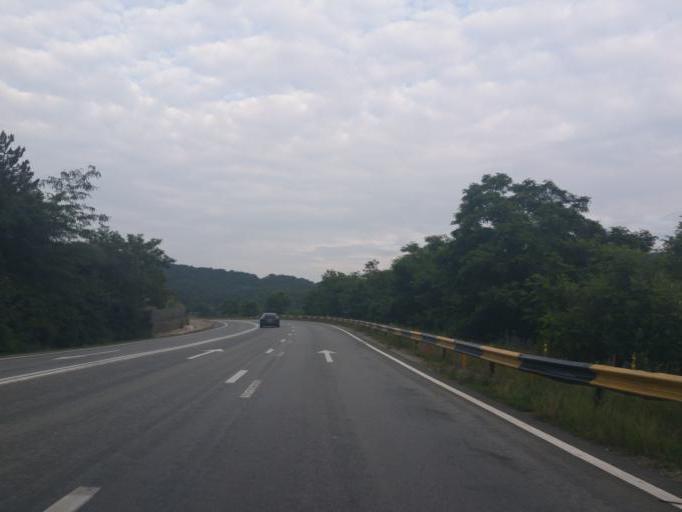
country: RO
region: Salaj
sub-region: Comuna Dragu
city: Dragu
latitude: 46.9467
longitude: 23.3682
